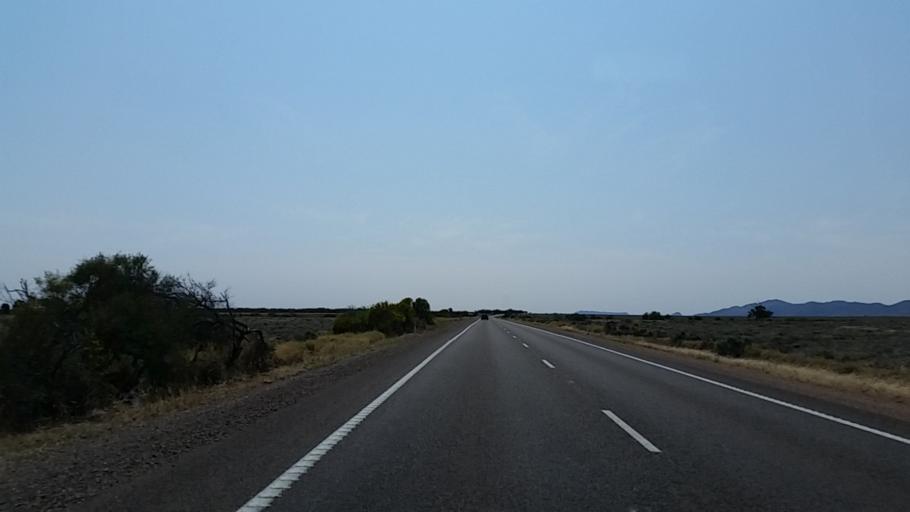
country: AU
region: South Australia
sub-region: Port Augusta
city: Port Augusta
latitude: -32.7325
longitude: 137.9409
